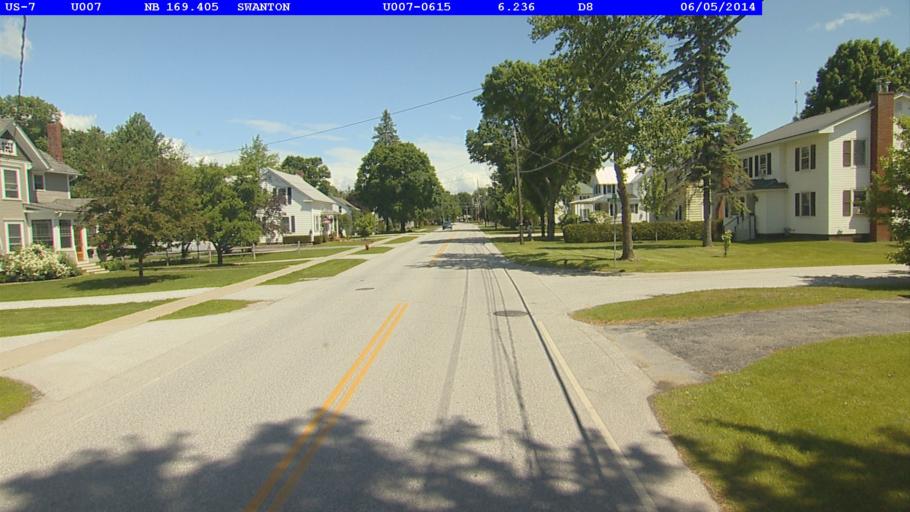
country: US
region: Vermont
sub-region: Franklin County
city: Swanton
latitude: 44.9229
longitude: -73.1209
